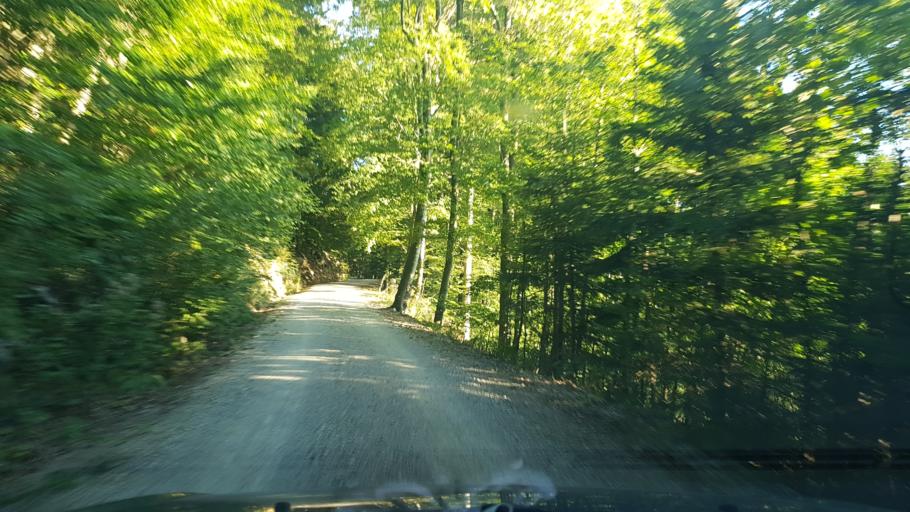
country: SI
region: Vipava
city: Vipava
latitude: 45.7834
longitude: 14.0397
